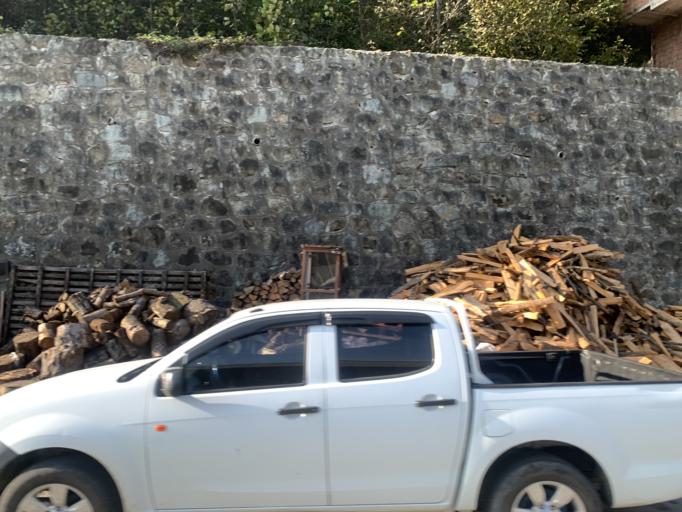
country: TR
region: Trabzon
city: Dernekpazari
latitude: 40.8397
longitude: 40.2790
